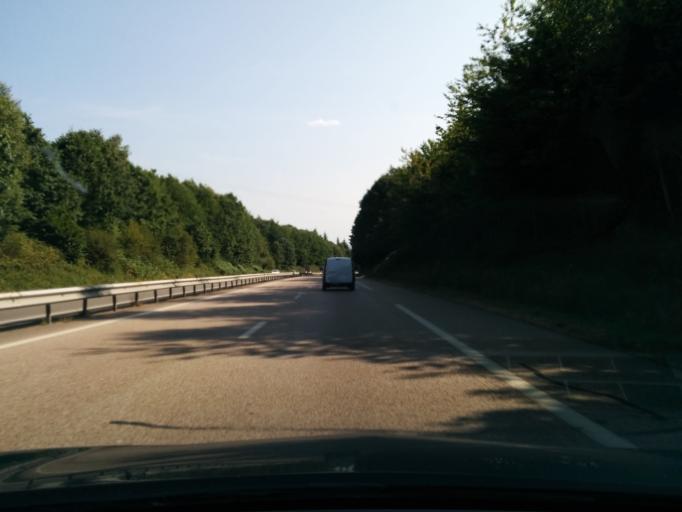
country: FR
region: Limousin
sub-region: Departement de la Haute-Vienne
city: Bonnac-la-Cote
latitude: 45.9511
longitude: 1.3154
